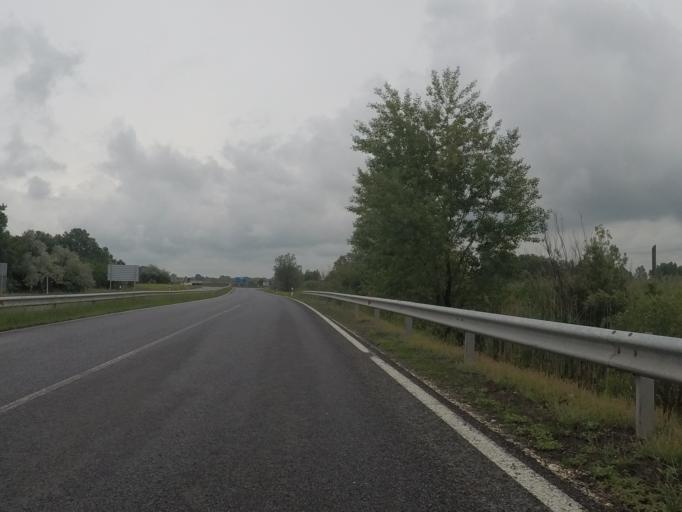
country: HU
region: Gyor-Moson-Sopron
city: Gyorujbarat
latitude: 47.6315
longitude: 17.6679
